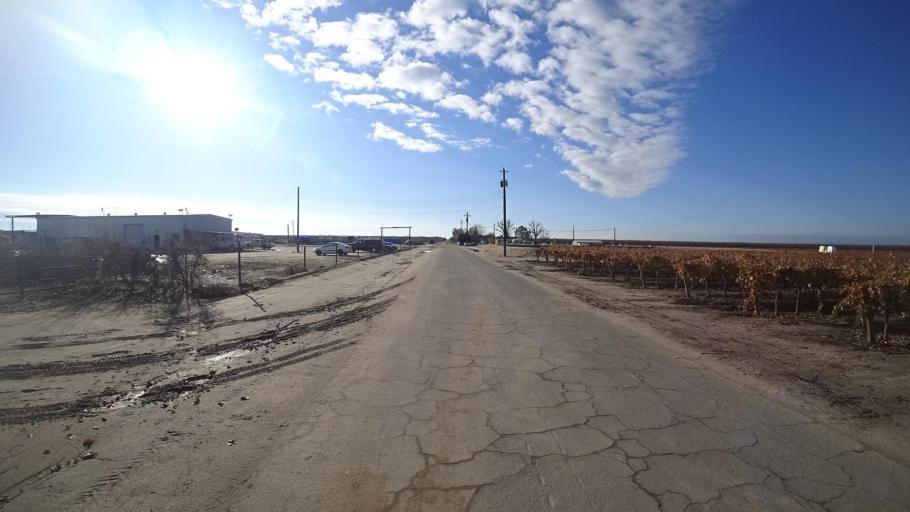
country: US
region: California
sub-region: Kern County
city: McFarland
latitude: 35.7047
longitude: -119.3030
